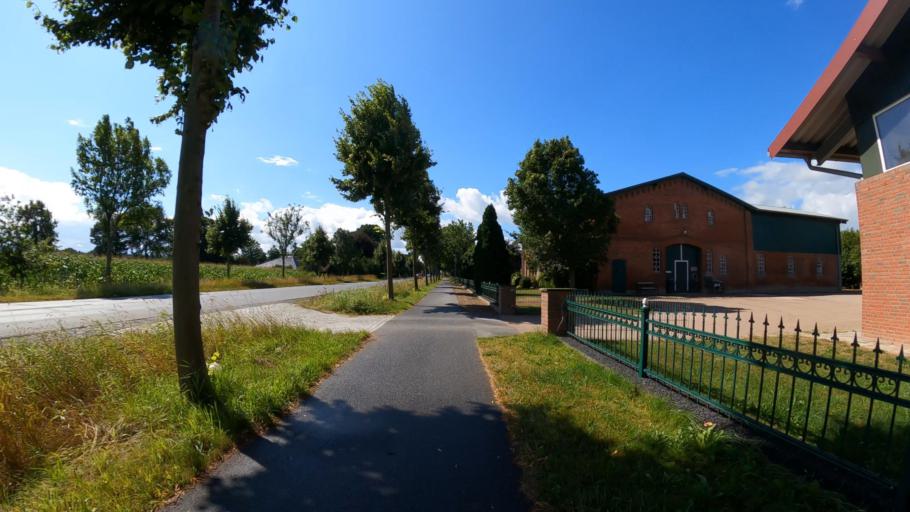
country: DE
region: Schleswig-Holstein
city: Wiemersdorf
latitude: 53.9523
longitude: 9.9006
